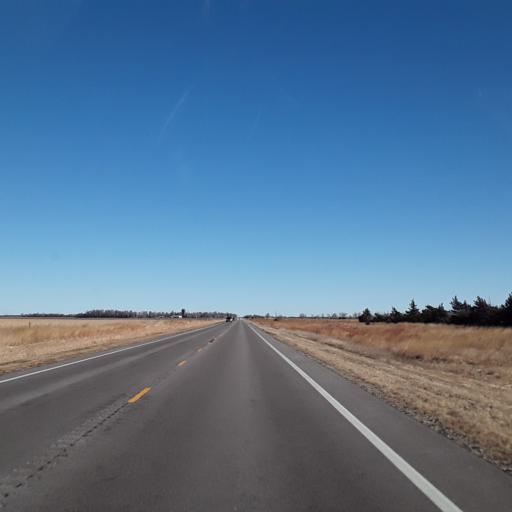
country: US
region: Kansas
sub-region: Pawnee County
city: Larned
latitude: 38.1054
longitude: -99.2003
